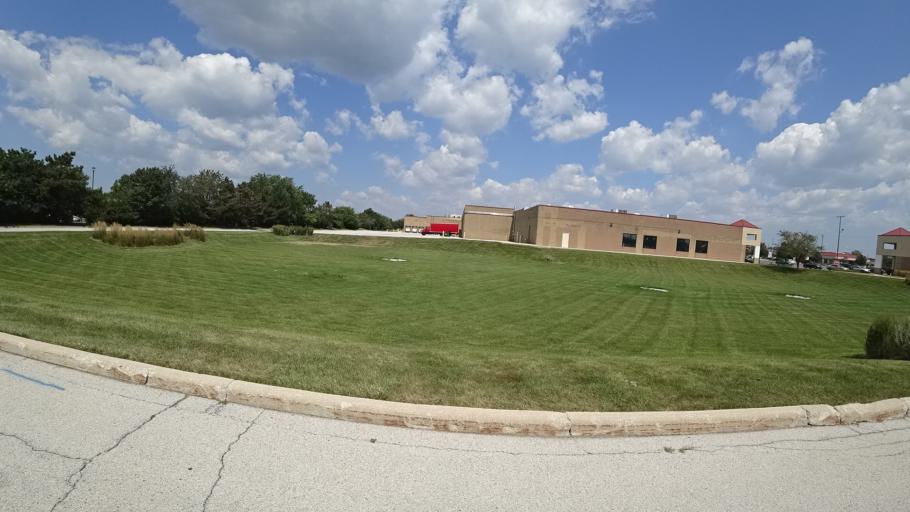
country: US
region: Illinois
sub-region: Cook County
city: Tinley Park
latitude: 41.5987
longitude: -87.7969
